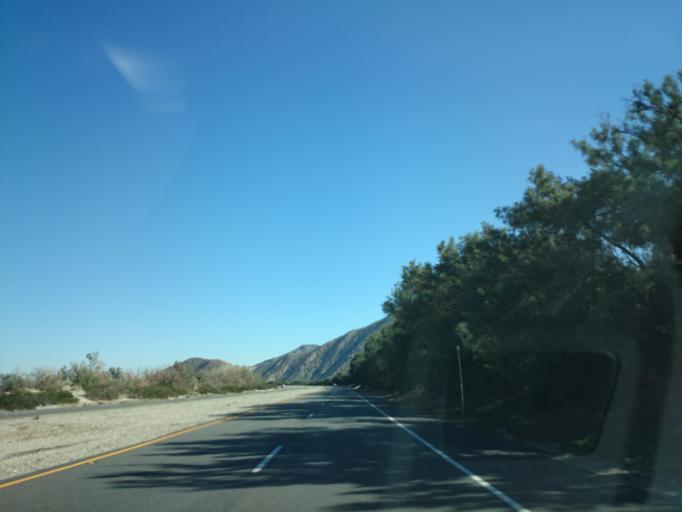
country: US
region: California
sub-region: Riverside County
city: Garnet
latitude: 33.9081
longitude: -116.6538
